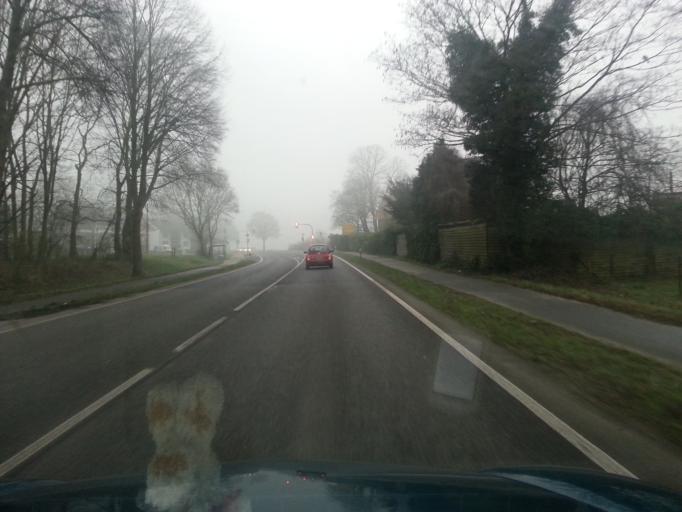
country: DE
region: North Rhine-Westphalia
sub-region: Regierungsbezirk Dusseldorf
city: Emmerich
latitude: 51.8102
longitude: 6.2030
